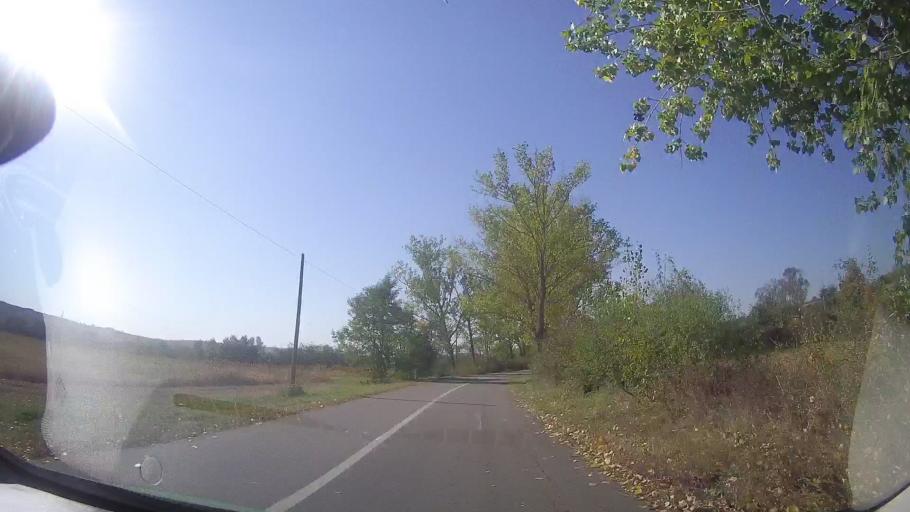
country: RO
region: Timis
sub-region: Comuna Secas
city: Secas
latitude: 45.8572
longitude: 21.8021
